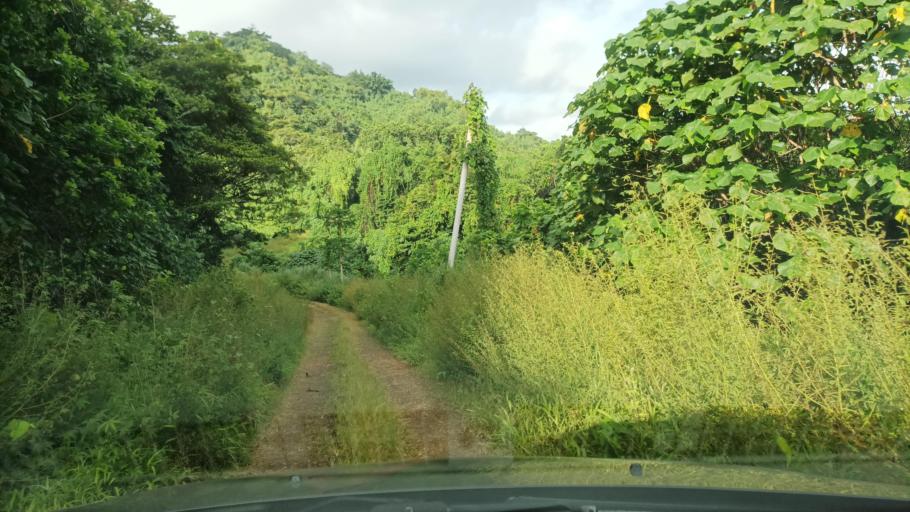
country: FM
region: Kosrae
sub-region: Utwe Municipality
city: Utwe
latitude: 5.2750
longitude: 162.9408
